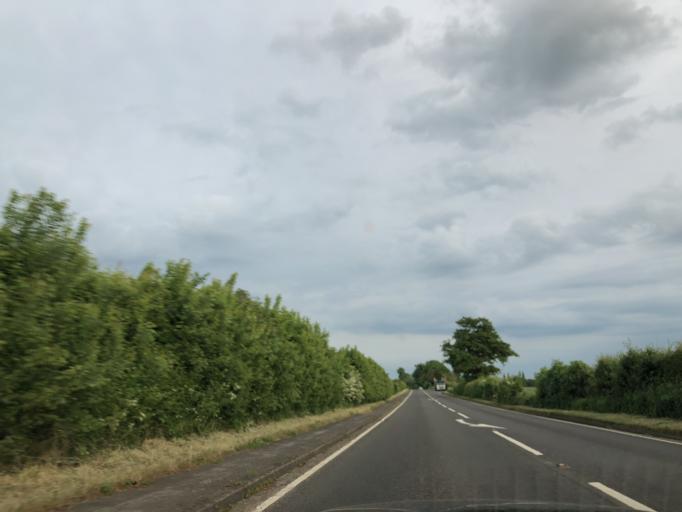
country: GB
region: England
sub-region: Warwickshire
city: Wroxall
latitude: 52.3126
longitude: -1.6657
